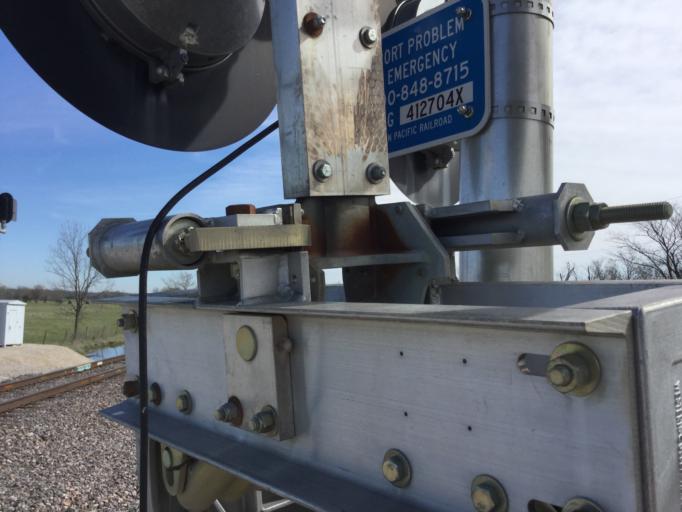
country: US
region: Kansas
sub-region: Neosho County
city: Erie
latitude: 37.6076
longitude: -95.2157
